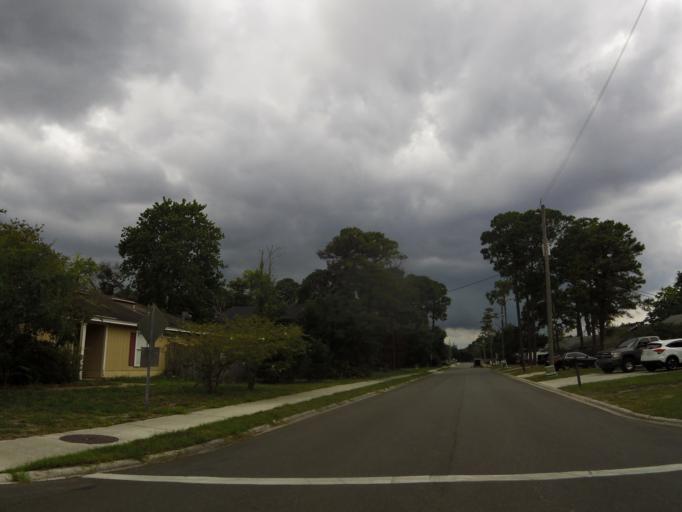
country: US
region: Florida
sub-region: Duval County
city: Atlantic Beach
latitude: 30.3312
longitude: -81.4194
